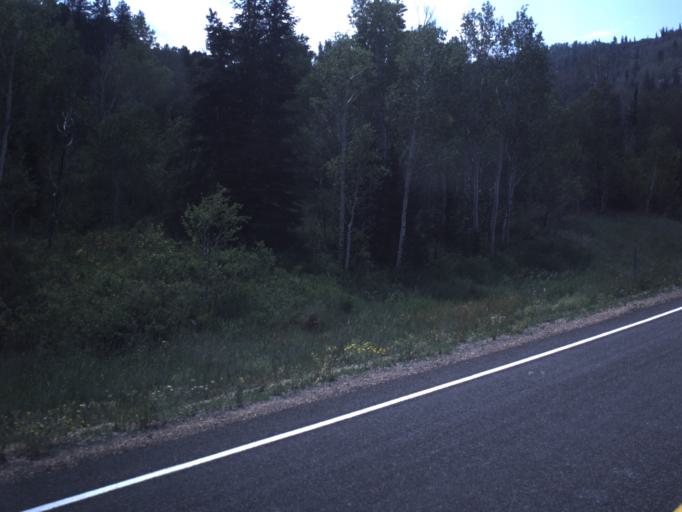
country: US
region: Utah
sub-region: Summit County
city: Francis
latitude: 40.5387
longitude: -111.0983
